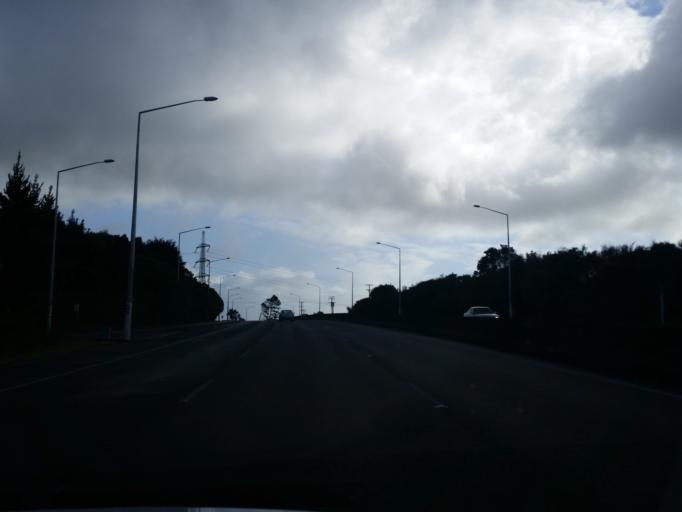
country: NZ
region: Auckland
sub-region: Auckland
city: Pukekohe East
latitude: -37.2141
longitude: 174.9994
